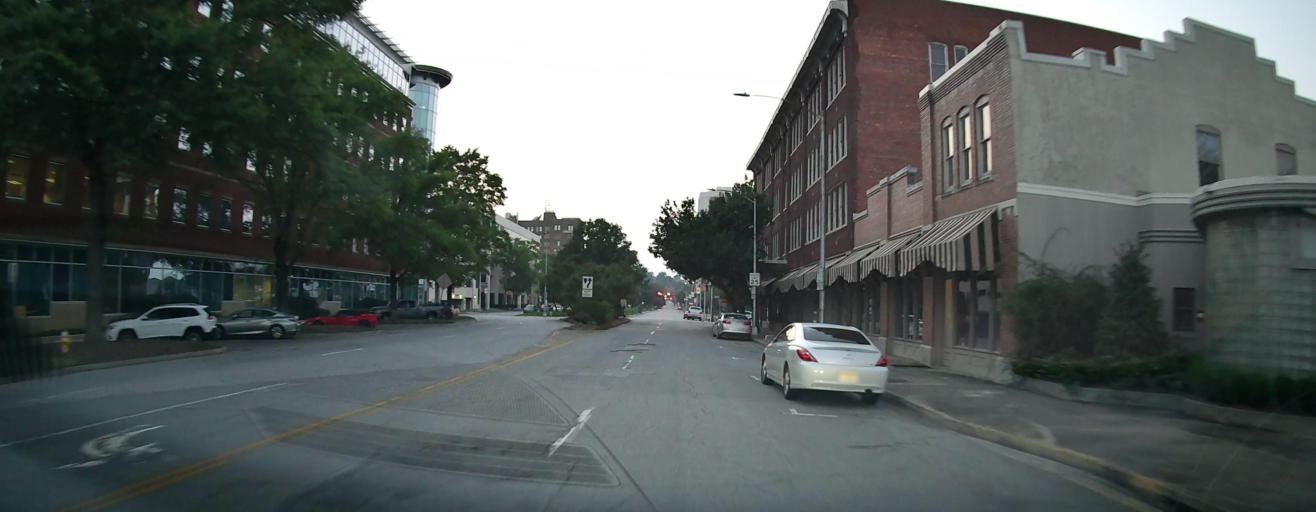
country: US
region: Georgia
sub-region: Bibb County
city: Macon
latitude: 32.8356
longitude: -83.6238
